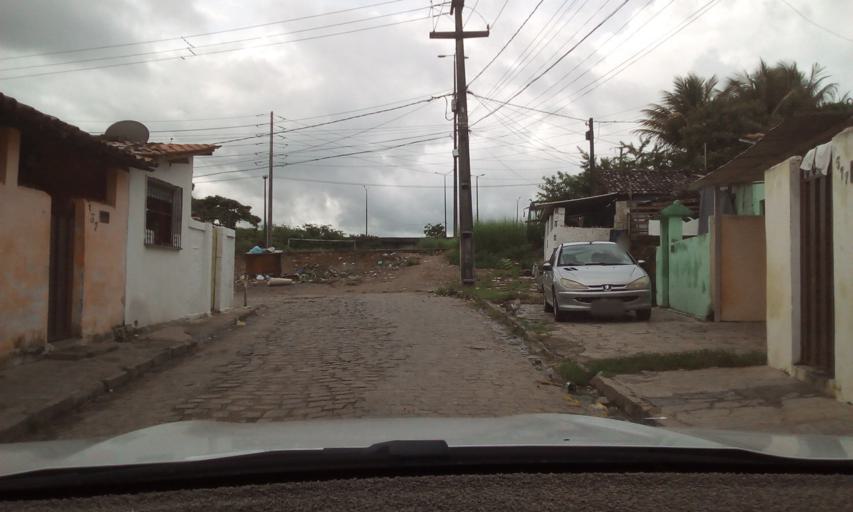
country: BR
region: Paraiba
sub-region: Joao Pessoa
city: Joao Pessoa
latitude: -7.1247
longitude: -34.8935
